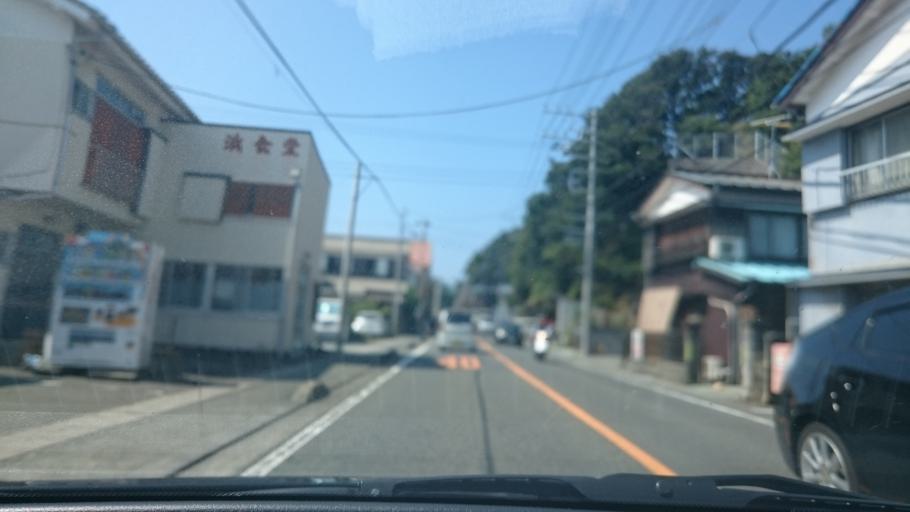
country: JP
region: Shizuoka
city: Heda
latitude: 34.7775
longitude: 138.7695
